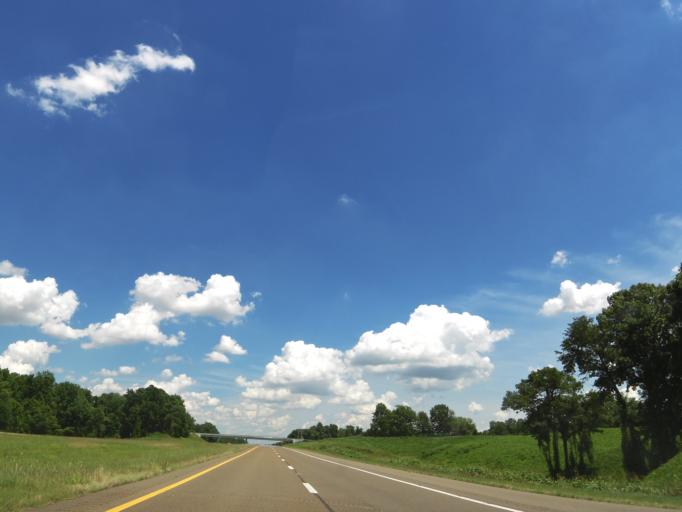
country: US
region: Tennessee
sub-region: Dyer County
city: Dyersburg
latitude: 36.0721
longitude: -89.4689
